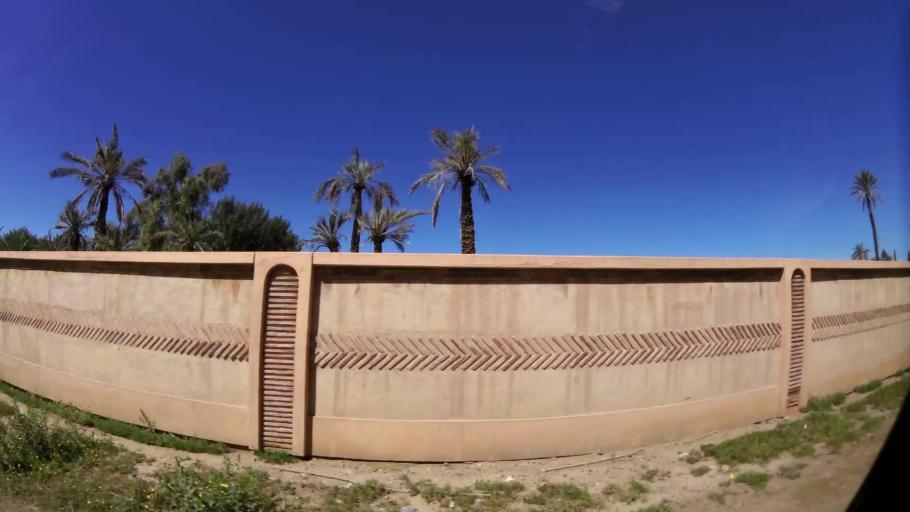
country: MA
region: Marrakech-Tensift-Al Haouz
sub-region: Marrakech
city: Marrakesh
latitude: 31.6663
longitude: -7.9602
